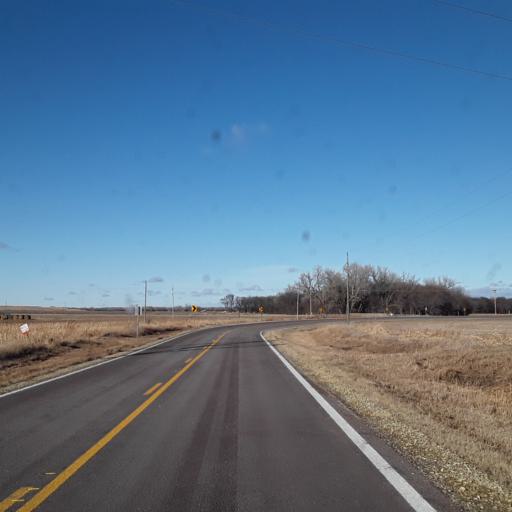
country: US
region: Kansas
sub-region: Cloud County
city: Concordia
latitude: 39.5638
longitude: -97.7229
